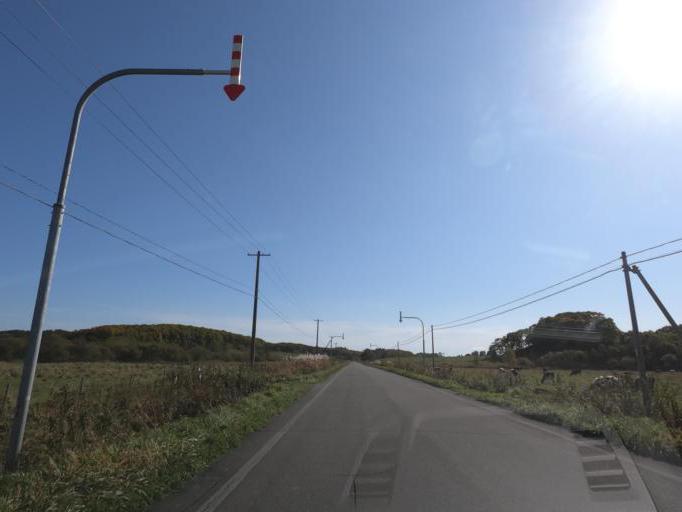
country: JP
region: Hokkaido
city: Obihiro
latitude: 42.7124
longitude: 143.4604
